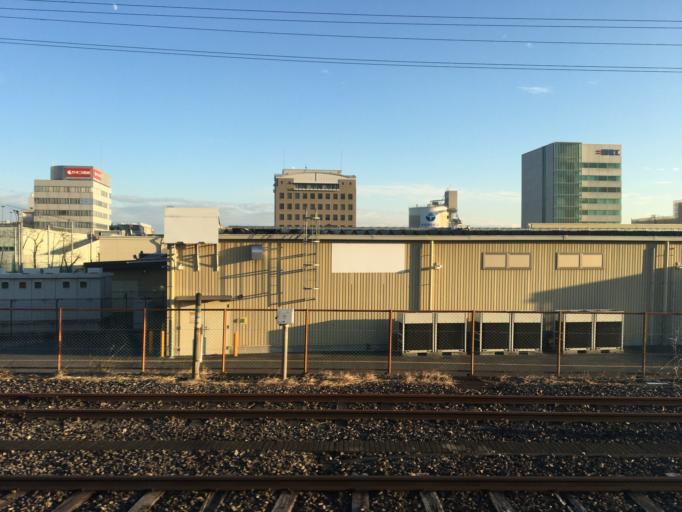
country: JP
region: Gunma
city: Maebashi-shi
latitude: 36.3772
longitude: 139.0448
